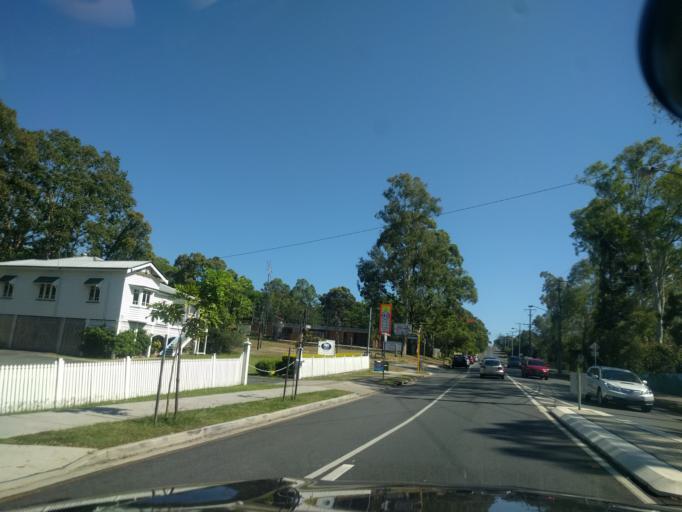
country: AU
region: Queensland
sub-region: Brisbane
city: Chermside West
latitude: -27.3813
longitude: 153.0131
